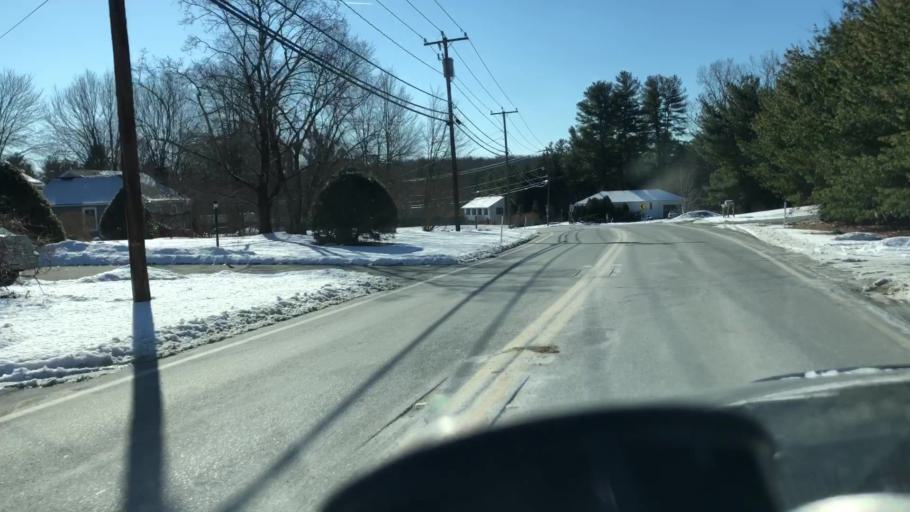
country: US
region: Massachusetts
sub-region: Hampshire County
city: Southampton
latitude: 42.2208
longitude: -72.7325
